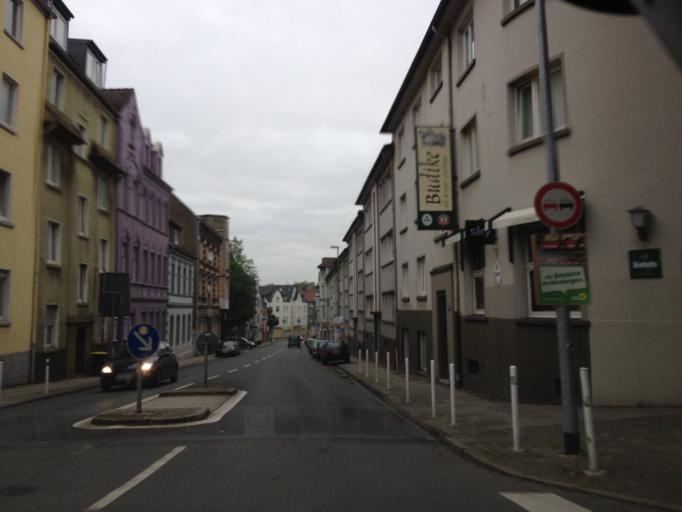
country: DE
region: North Rhine-Westphalia
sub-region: Regierungsbezirk Dusseldorf
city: Essen
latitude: 51.4592
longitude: 7.0743
